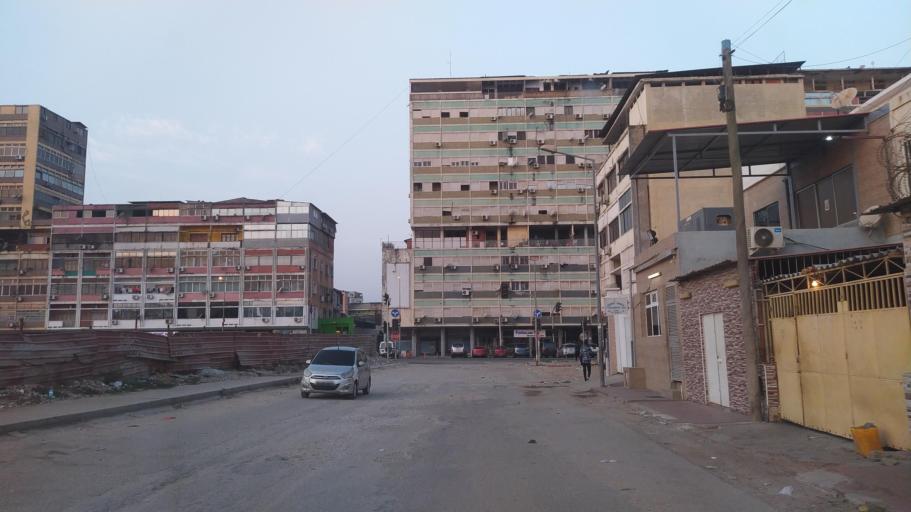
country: AO
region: Luanda
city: Luanda
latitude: -8.8181
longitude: 13.2495
